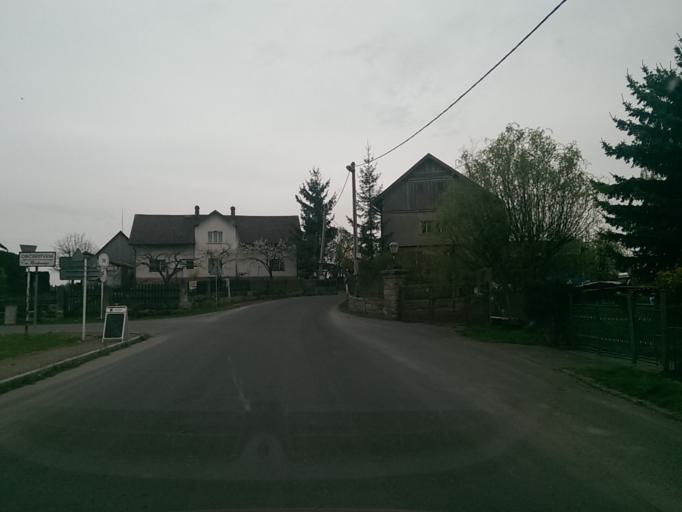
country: CZ
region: Central Bohemia
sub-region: Okres Mlada Boleslav
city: Zd'ar
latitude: 50.5569
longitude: 15.1055
